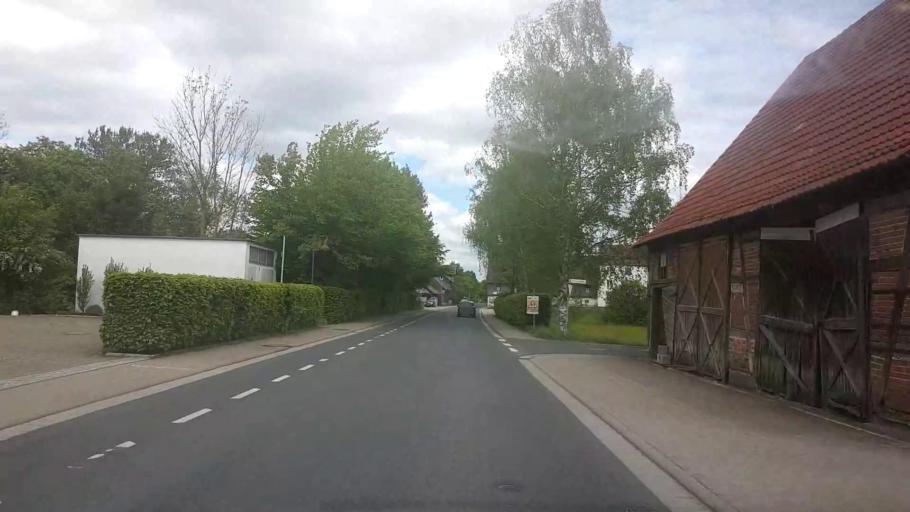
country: DE
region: Bavaria
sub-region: Upper Franconia
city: Untersiemau
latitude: 50.2048
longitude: 10.9750
